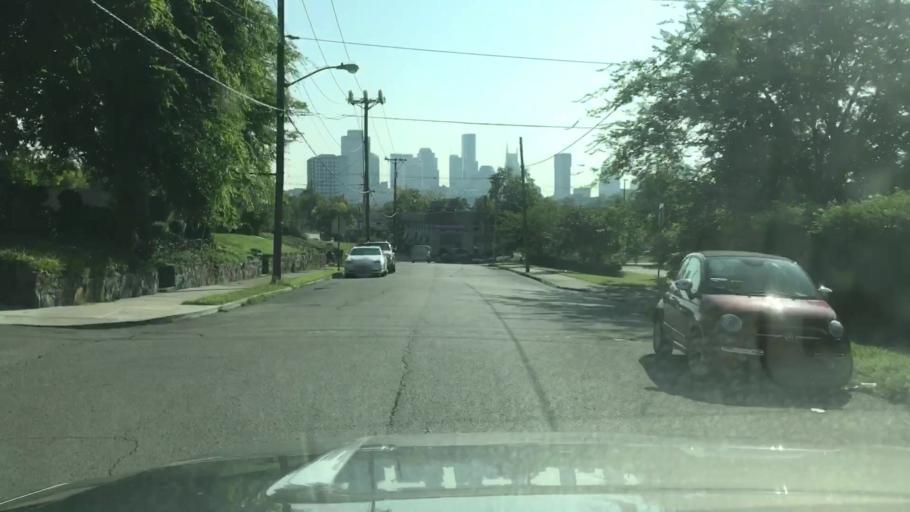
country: US
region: Tennessee
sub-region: Davidson County
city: Nashville
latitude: 36.1586
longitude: -86.8021
